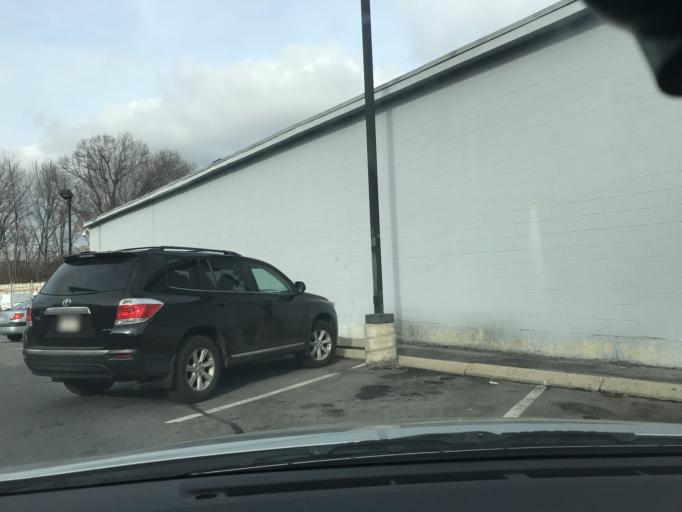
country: US
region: Massachusetts
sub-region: Middlesex County
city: Lowell
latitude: 42.6376
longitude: -71.3458
